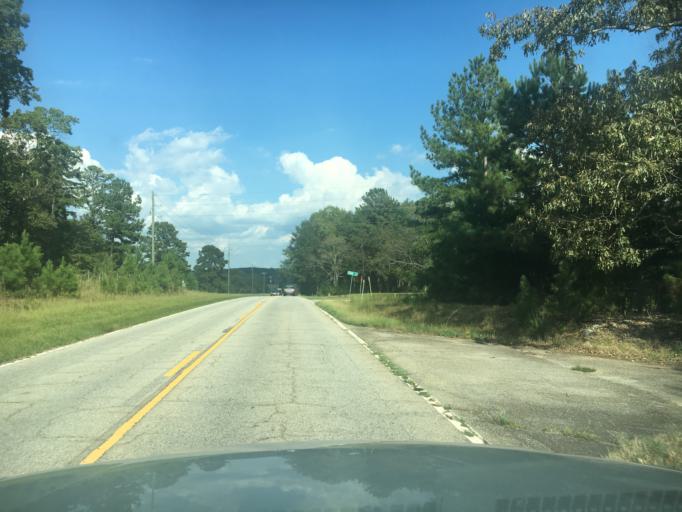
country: US
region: South Carolina
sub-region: Pickens County
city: Central
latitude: 34.7012
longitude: -82.7313
